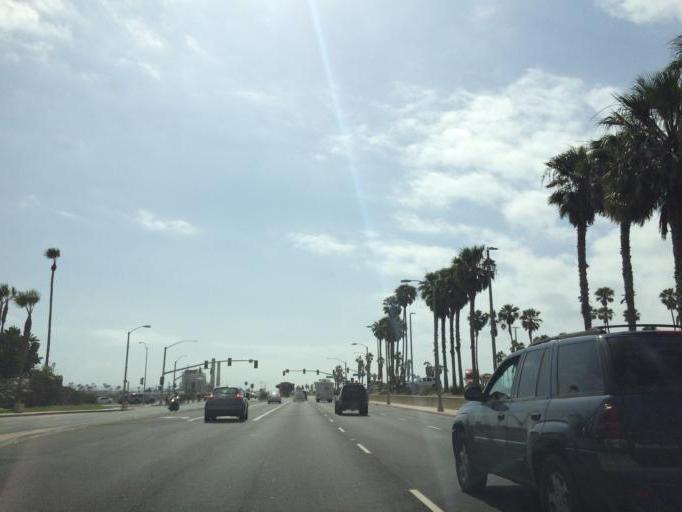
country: US
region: California
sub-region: Orange County
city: Huntington Beach
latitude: 33.6493
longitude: -117.9895
